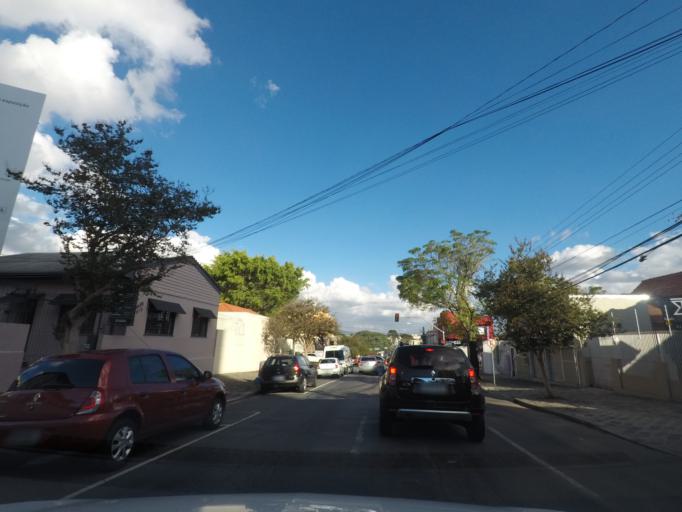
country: BR
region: Parana
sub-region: Curitiba
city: Curitiba
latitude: -25.4455
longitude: -49.2703
